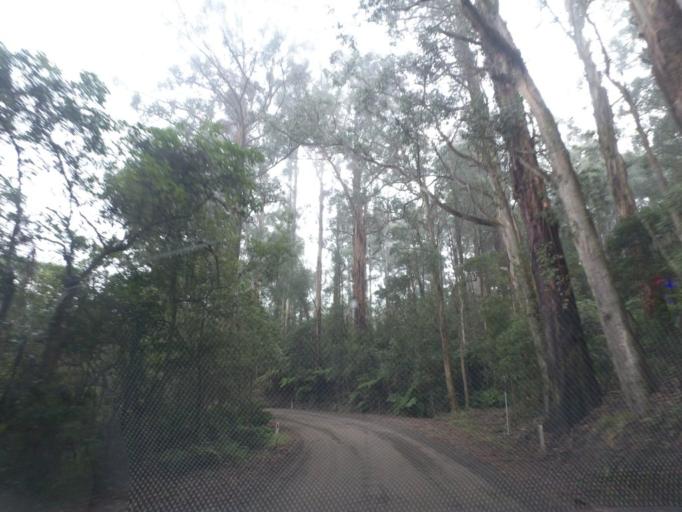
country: AU
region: Victoria
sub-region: Yarra Ranges
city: Badger Creek
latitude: -37.7033
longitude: 145.5804
